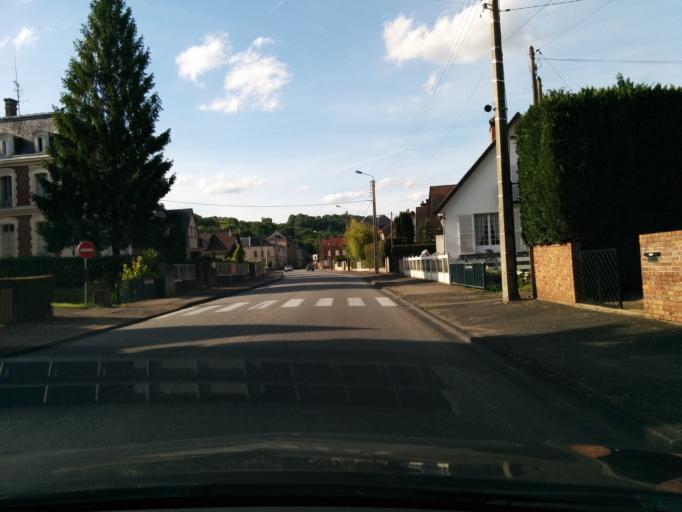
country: FR
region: Haute-Normandie
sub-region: Departement de l'Eure
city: Les Andelys
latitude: 49.2463
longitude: 1.4138
